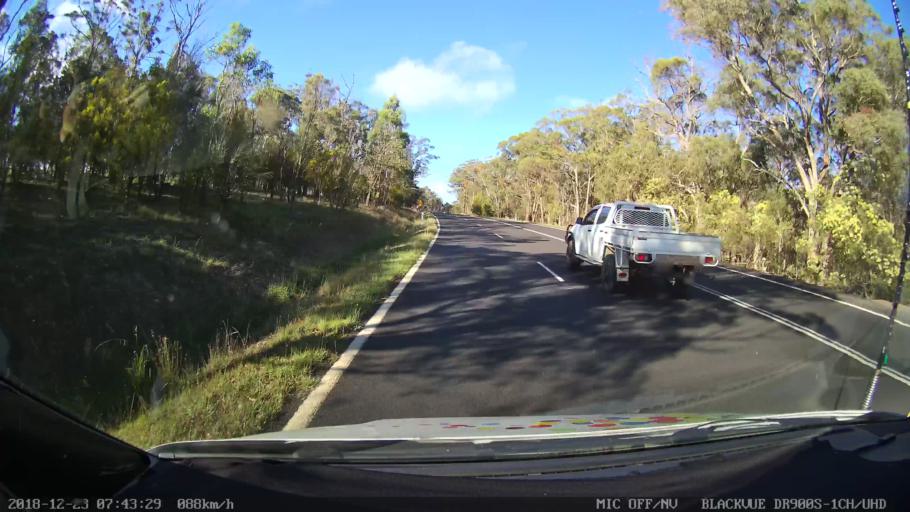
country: AU
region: New South Wales
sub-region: Armidale Dumaresq
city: Enmore
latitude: -30.5224
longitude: 151.9635
